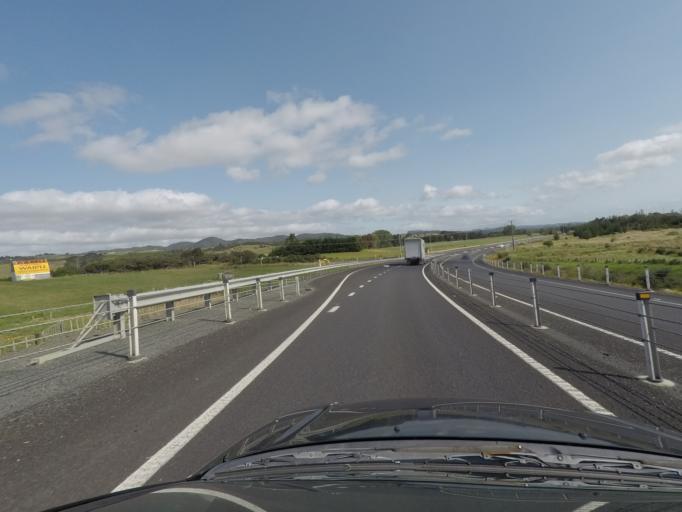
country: NZ
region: Northland
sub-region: Whangarei
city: Ruakaka
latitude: -36.0343
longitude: 174.4151
